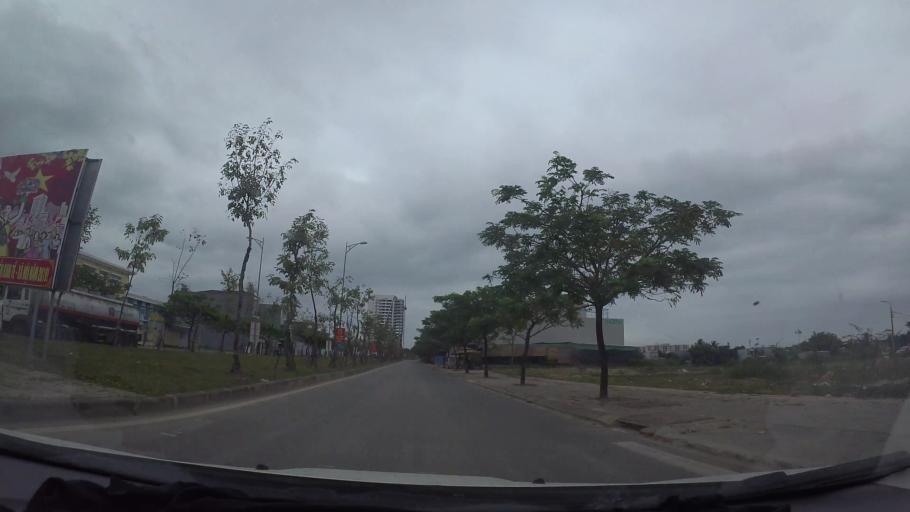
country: VN
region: Da Nang
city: Lien Chieu
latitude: 16.1068
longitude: 108.1265
